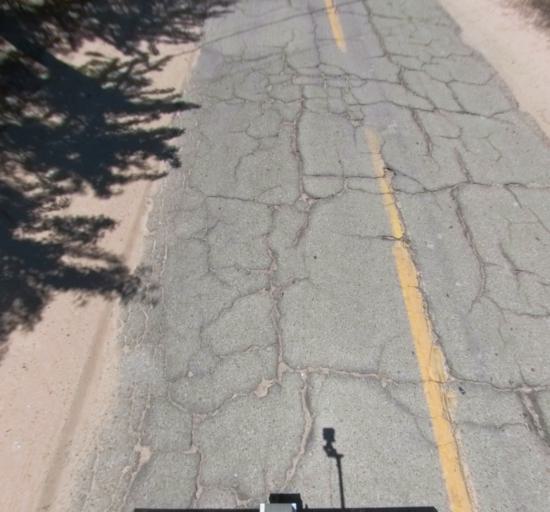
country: US
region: California
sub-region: Madera County
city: Fairmead
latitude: 36.9964
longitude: -120.1984
